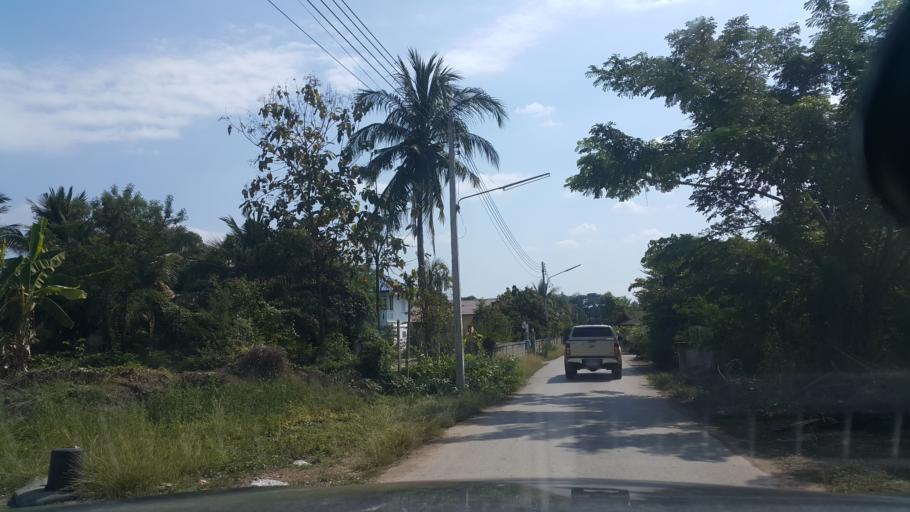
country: TH
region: Sukhothai
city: Thung Saliam
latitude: 17.3193
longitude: 99.5722
